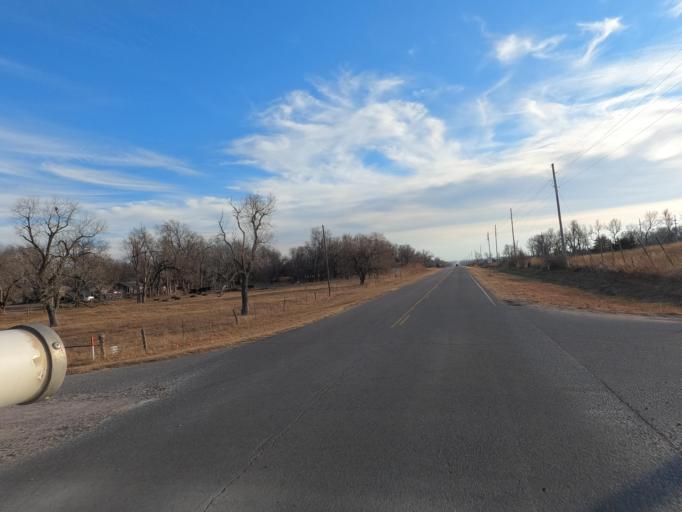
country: US
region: Kansas
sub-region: Reno County
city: Buhler
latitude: 38.0575
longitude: -97.7751
